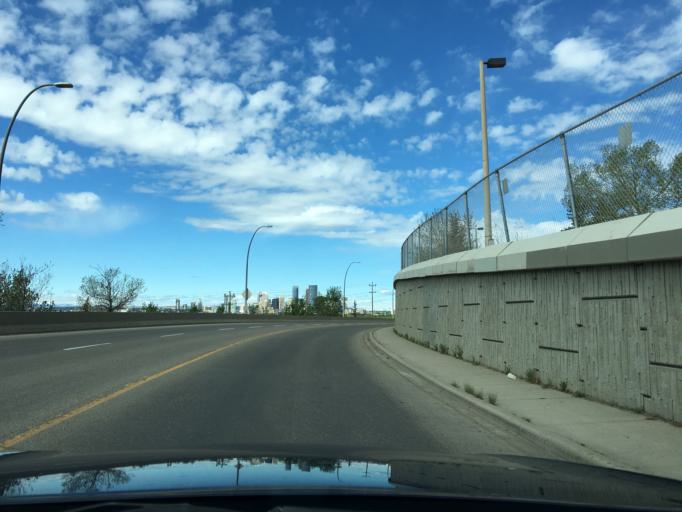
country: CA
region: Alberta
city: Calgary
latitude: 51.0379
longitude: -113.9985
